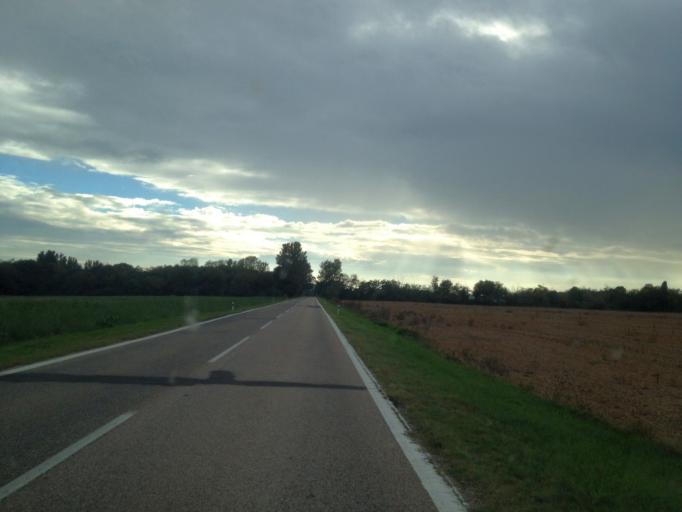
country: HU
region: Komarom-Esztergom
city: Sutto
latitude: 47.7672
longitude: 18.4221
